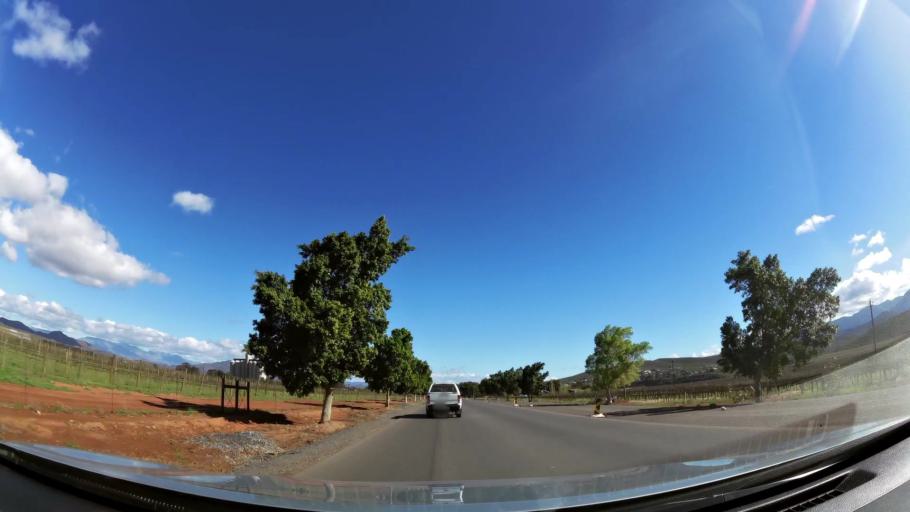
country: ZA
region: Western Cape
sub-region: Cape Winelands District Municipality
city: Ashton
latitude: -33.8310
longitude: 20.0785
